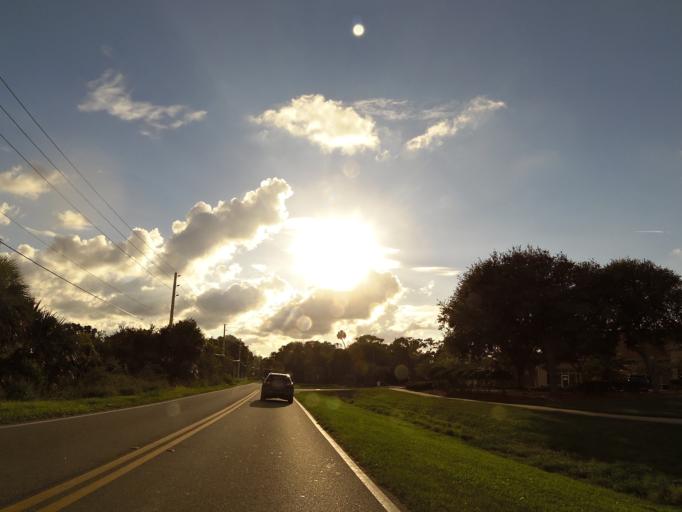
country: US
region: Florida
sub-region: Saint Johns County
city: Palm Valley
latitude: 30.1608
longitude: -81.3611
